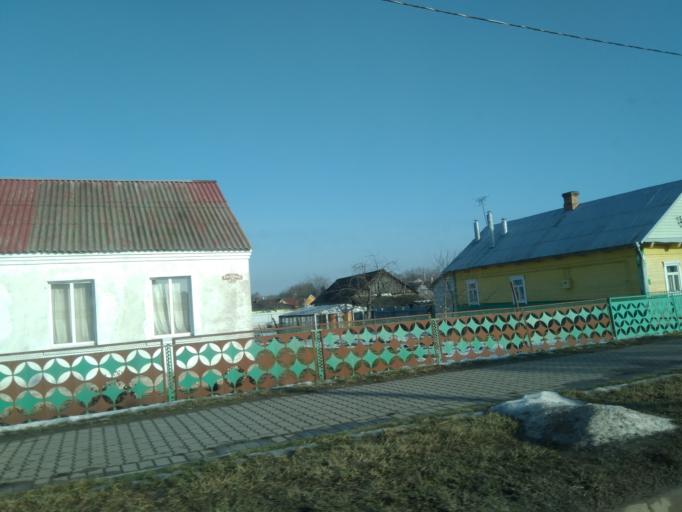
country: BY
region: Minsk
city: Snow
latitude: 53.2233
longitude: 26.3983
